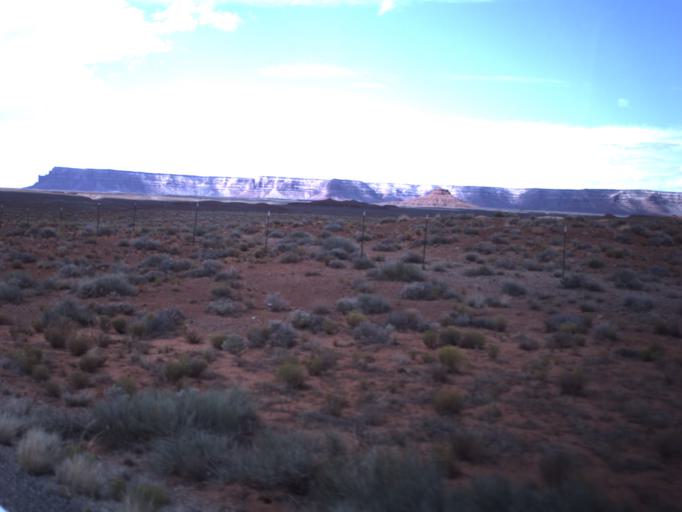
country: US
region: Utah
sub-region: San Juan County
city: Blanding
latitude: 37.2169
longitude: -109.8347
